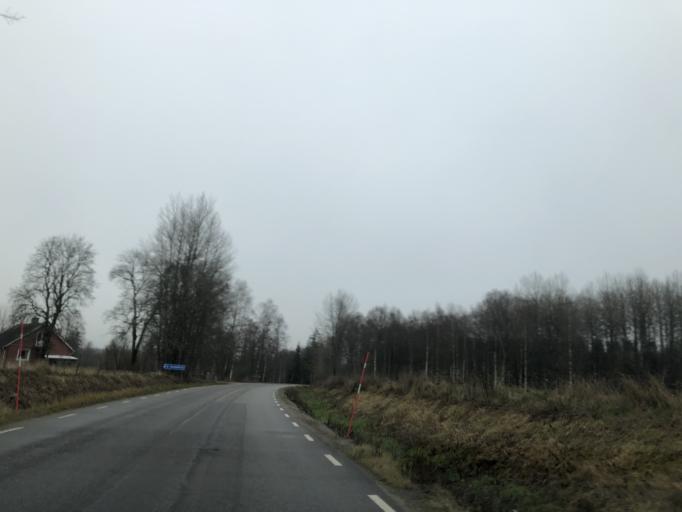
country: SE
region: Vaestra Goetaland
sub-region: Ulricehamns Kommun
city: Ulricehamn
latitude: 57.7164
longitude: 13.5211
